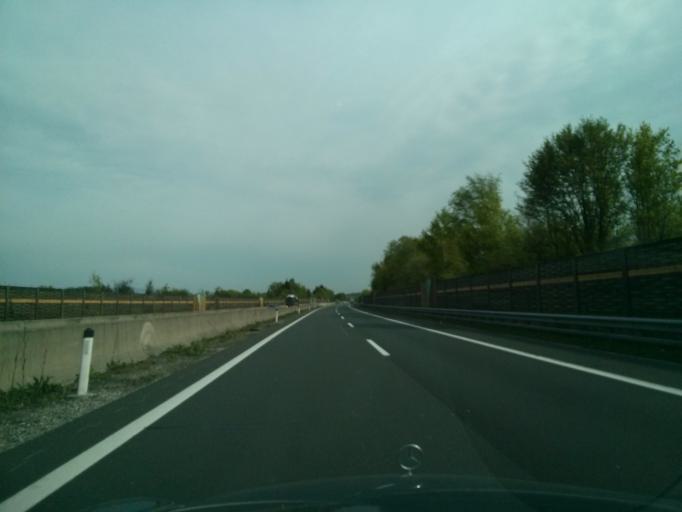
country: AT
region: Styria
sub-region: Politischer Bezirk Hartberg-Fuerstenfeld
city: Sankt Johann in der Haide
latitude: 47.2428
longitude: 15.9967
